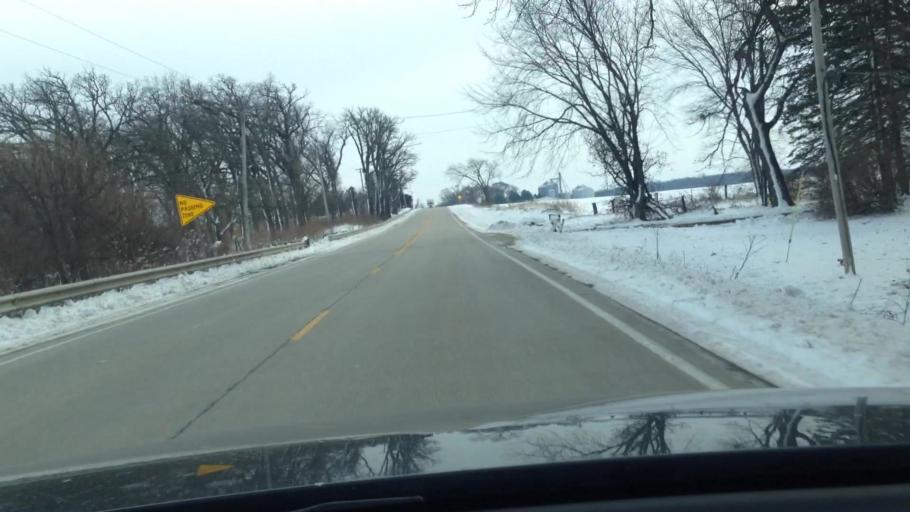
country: US
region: Illinois
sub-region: McHenry County
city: Hebron
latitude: 42.4073
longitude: -88.4385
